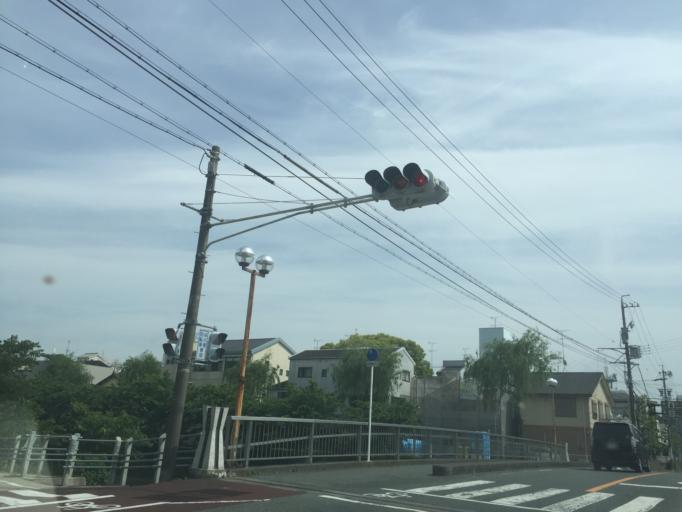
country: JP
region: Shizuoka
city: Kakegawa
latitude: 34.7745
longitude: 138.0135
